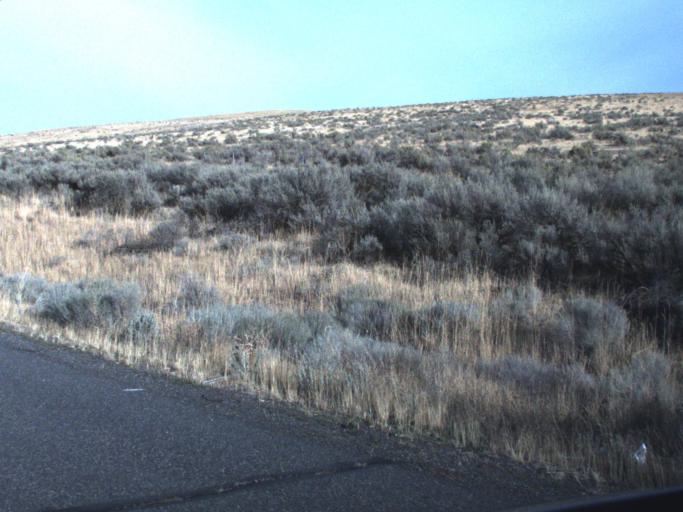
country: US
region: Oregon
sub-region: Umatilla County
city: Umatilla
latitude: 45.9888
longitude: -119.2987
